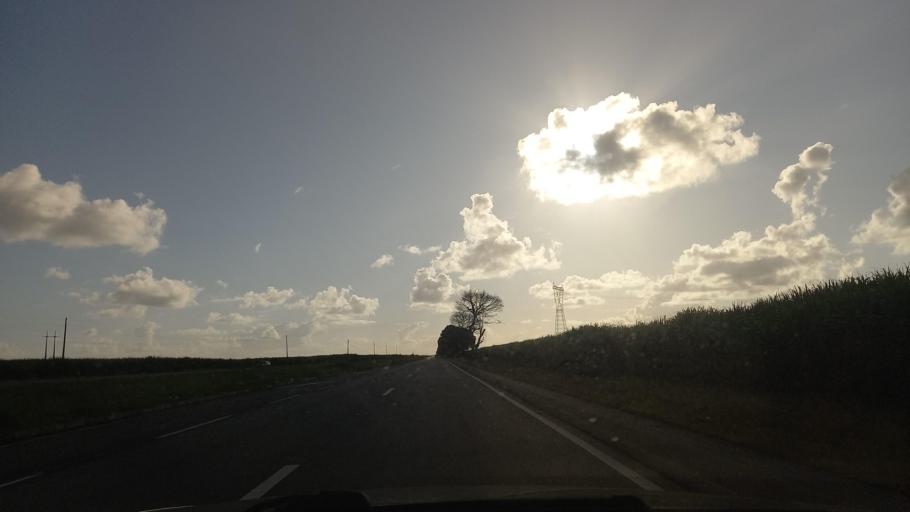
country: BR
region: Alagoas
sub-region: Sao Miguel Dos Campos
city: Sao Miguel dos Campos
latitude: -9.8036
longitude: -36.1378
